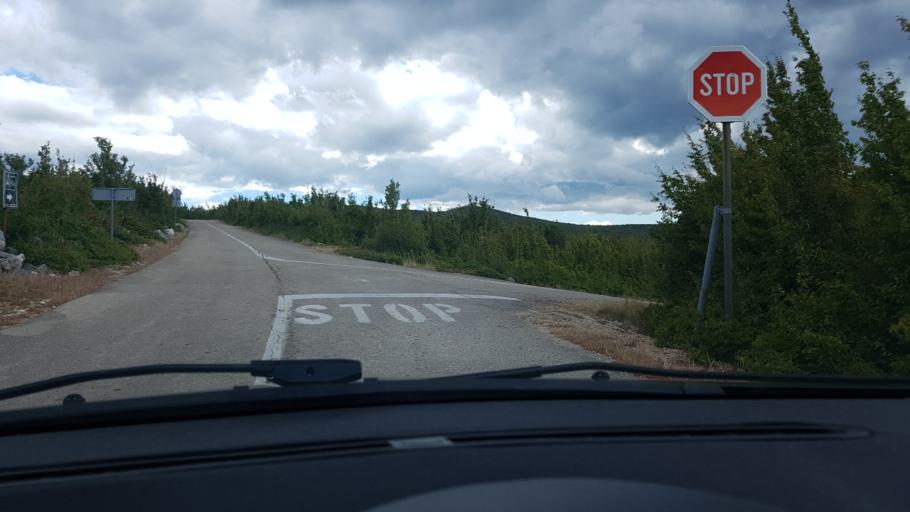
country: HR
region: Zadarska
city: Gracac
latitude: 44.1839
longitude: 15.8898
